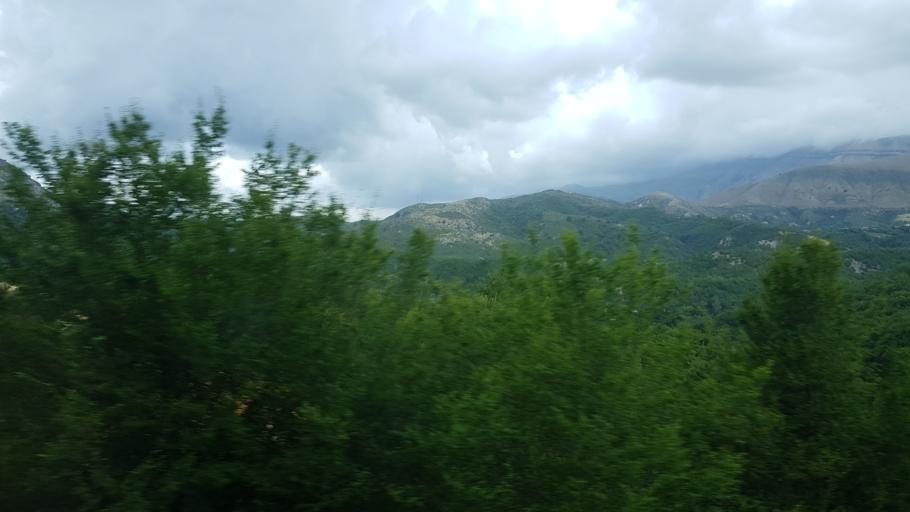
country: AL
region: Vlore
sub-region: Rrethi i Sarandes
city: Dhiver
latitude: 39.9132
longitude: 20.1911
